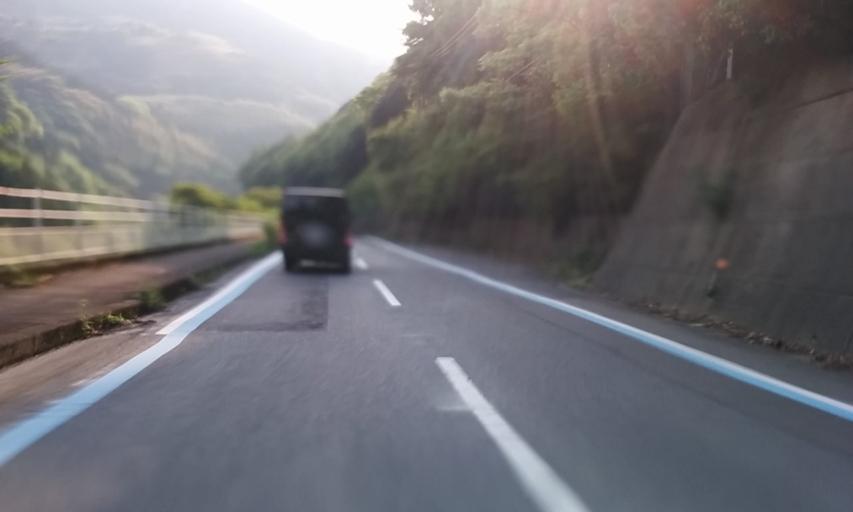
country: JP
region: Ehime
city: Saijo
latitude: 33.8664
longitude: 133.1901
